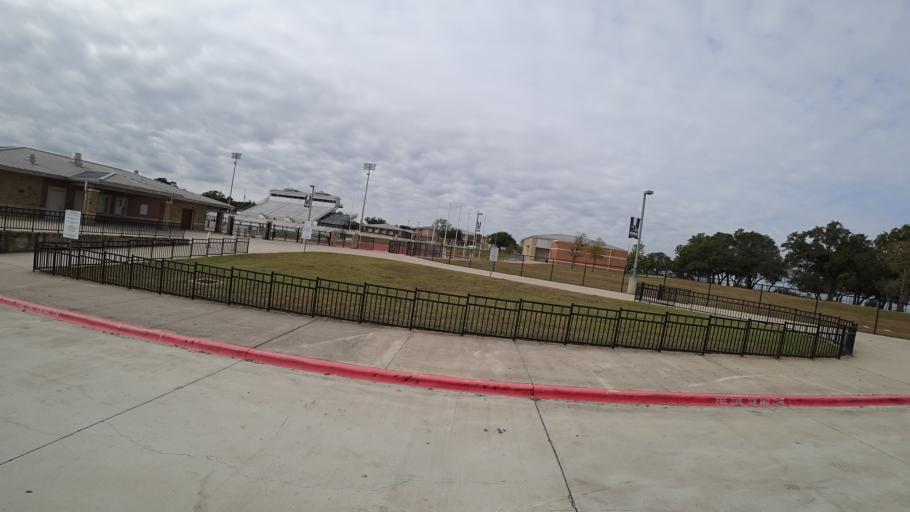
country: US
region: Texas
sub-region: Williamson County
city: Anderson Mill
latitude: 30.3972
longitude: -97.8267
